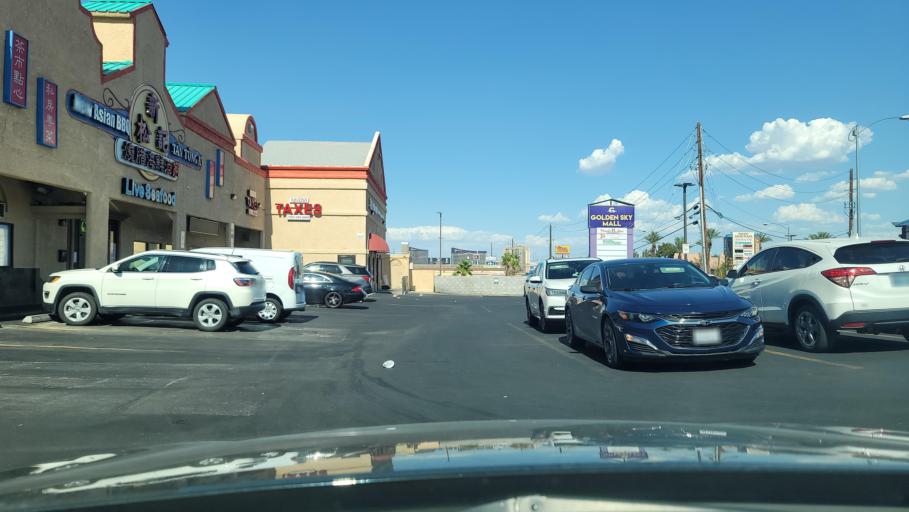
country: US
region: Nevada
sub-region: Clark County
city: Spring Valley
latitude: 36.1263
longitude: -115.2120
